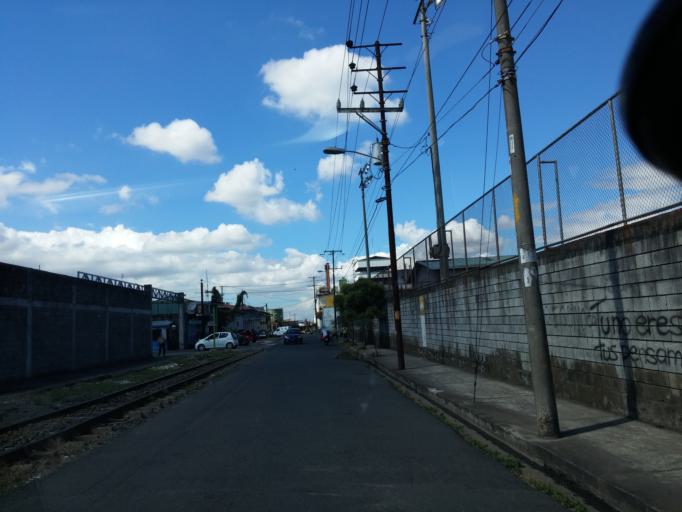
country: CR
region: San Jose
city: San Jose
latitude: 9.9252
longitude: -84.0883
